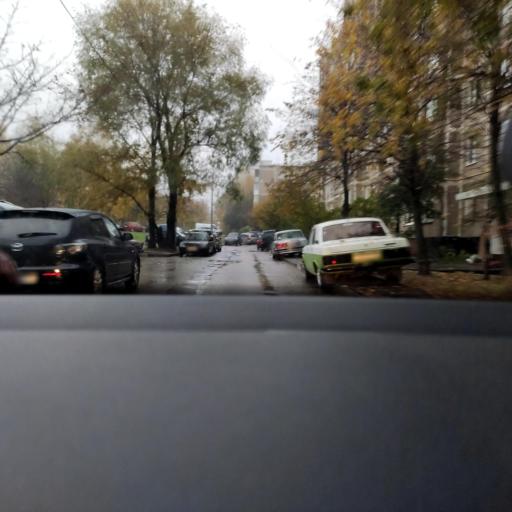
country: RU
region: Moskovskaya
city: Shcherbinka
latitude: 55.5375
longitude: 37.5786
